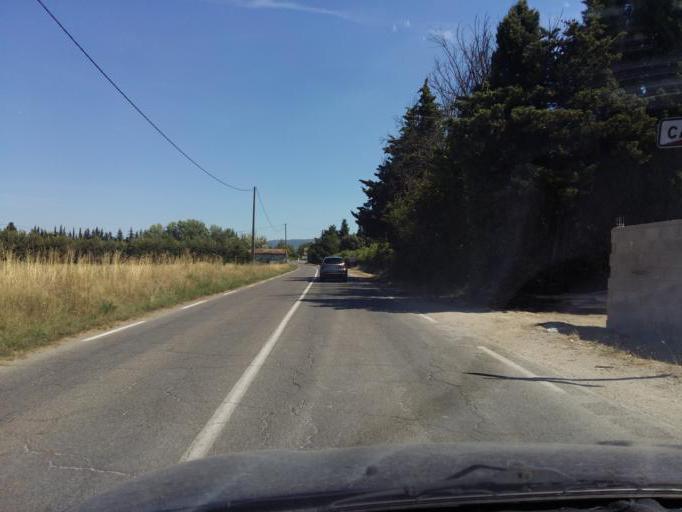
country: FR
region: Provence-Alpes-Cote d'Azur
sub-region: Departement du Vaucluse
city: Carpentras
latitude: 44.0446
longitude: 5.0606
